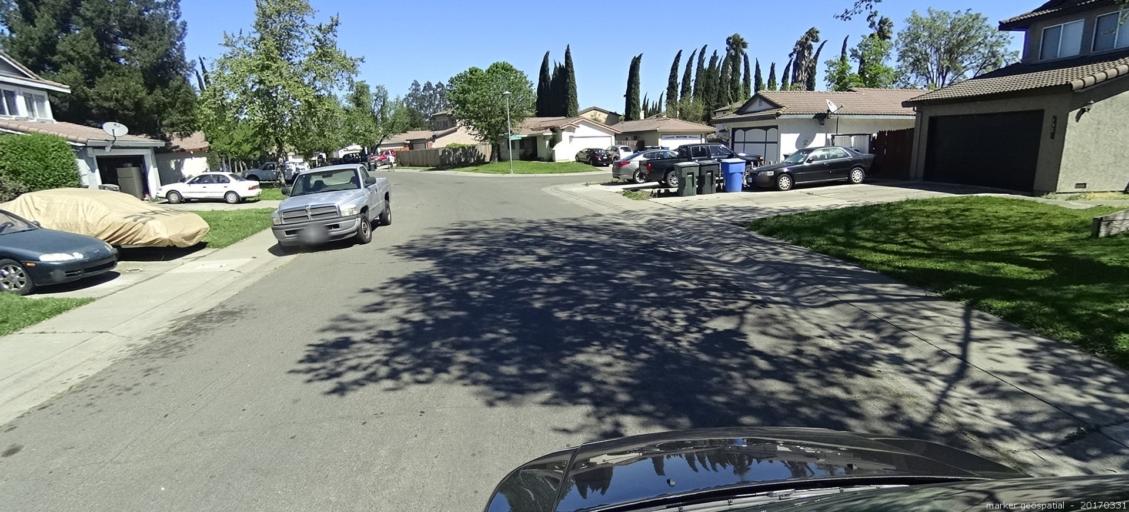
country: US
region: California
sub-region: Sacramento County
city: Parkway
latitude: 38.4625
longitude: -121.4414
